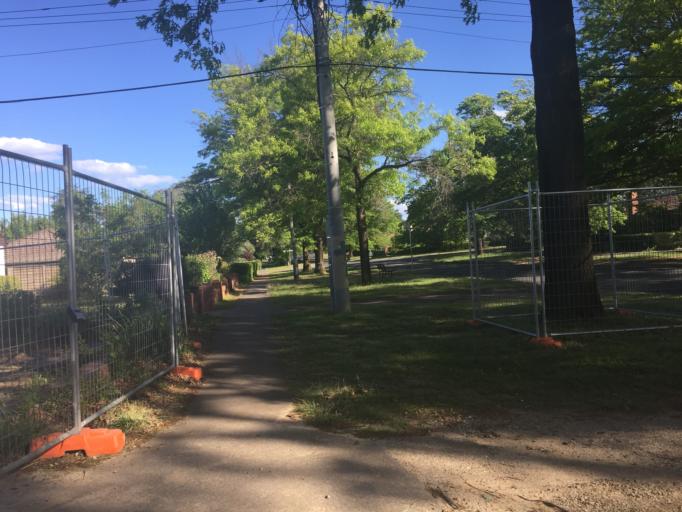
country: AU
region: Australian Capital Territory
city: Forrest
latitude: -35.3234
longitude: 149.1377
